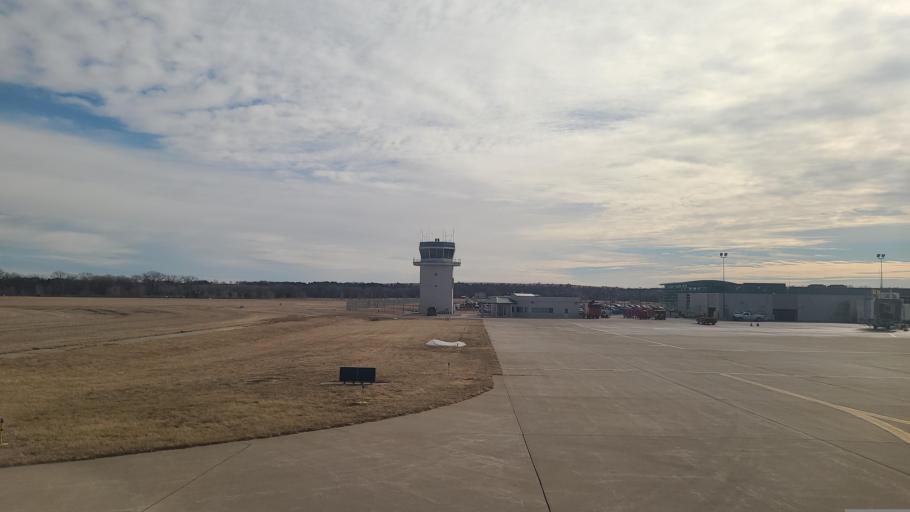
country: US
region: Kansas
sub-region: Riley County
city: Ogden
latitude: 39.1387
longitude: -96.6708
